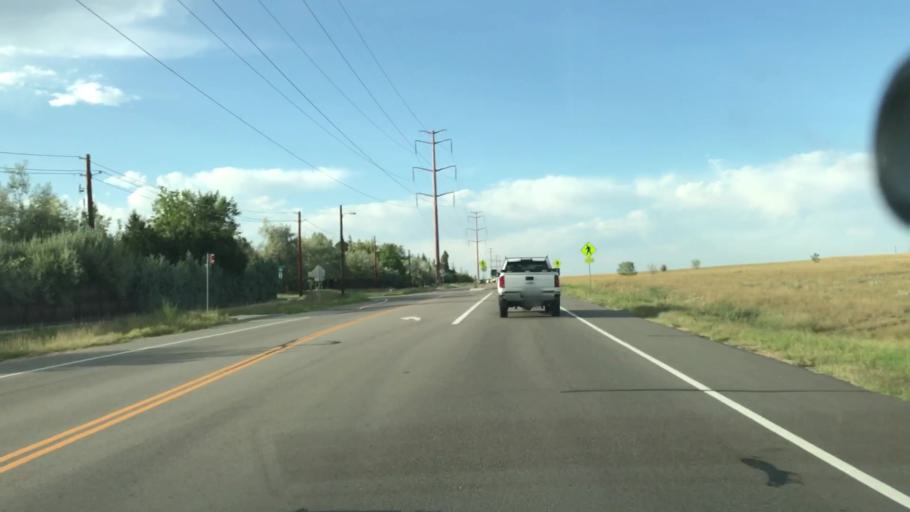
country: US
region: Colorado
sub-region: Boulder County
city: Gunbarrel
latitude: 40.0618
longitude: -105.1784
